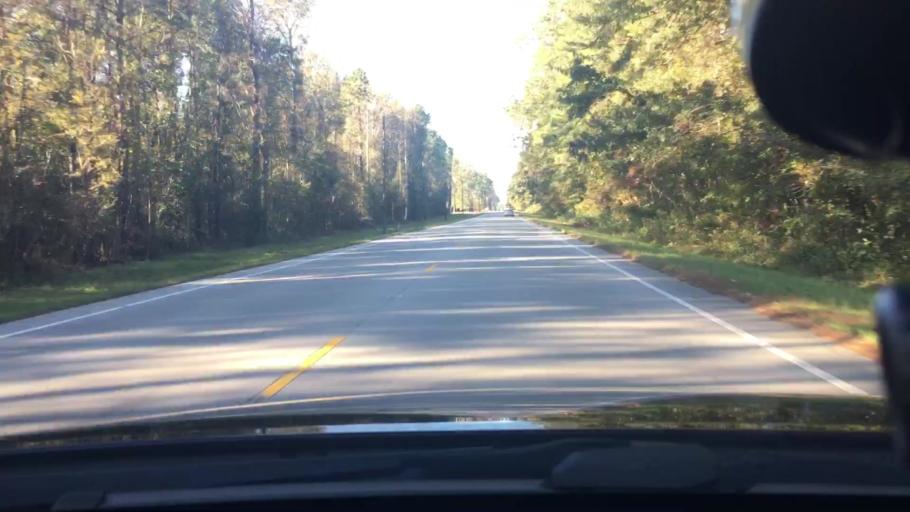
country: US
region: North Carolina
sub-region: Craven County
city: New Bern
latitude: 35.2009
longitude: -77.0569
